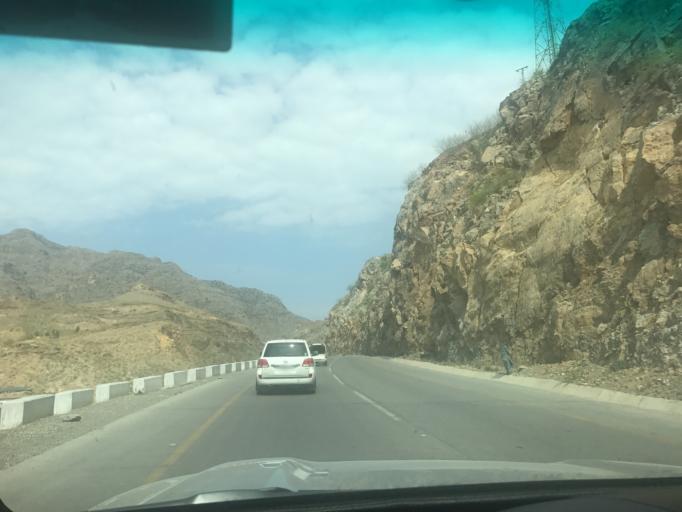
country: PK
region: Federally Administered Tribal Areas
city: Landi Kotal
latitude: 34.0231
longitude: 71.2632
